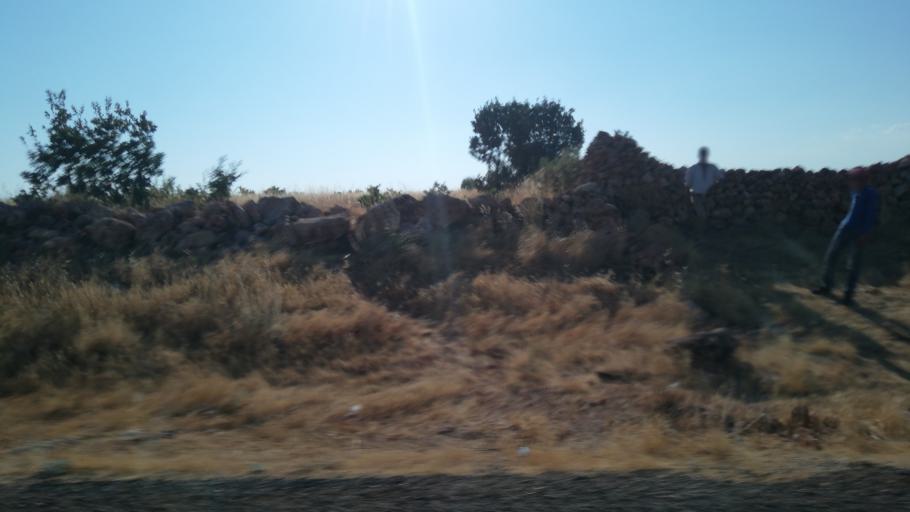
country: TR
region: Mardin
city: Sivrice
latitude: 37.2909
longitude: 41.3578
